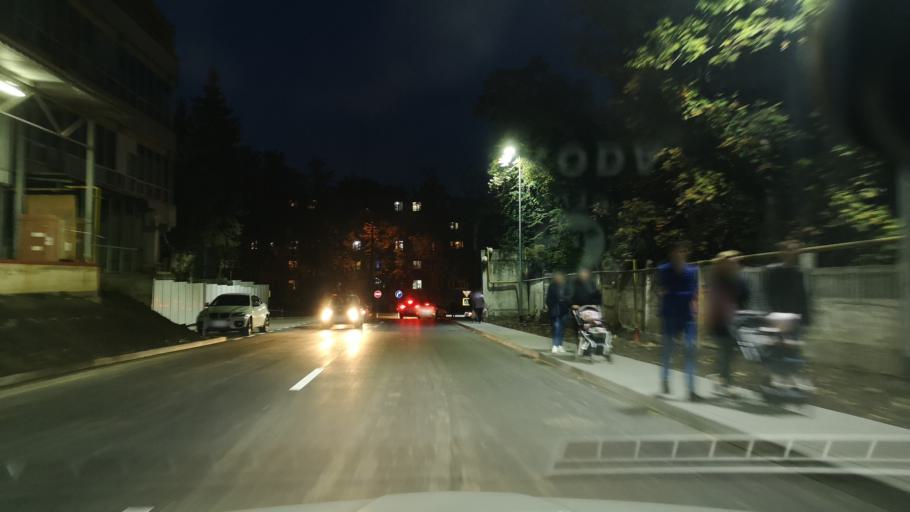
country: MD
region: Chisinau
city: Chisinau
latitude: 46.9918
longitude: 28.8618
